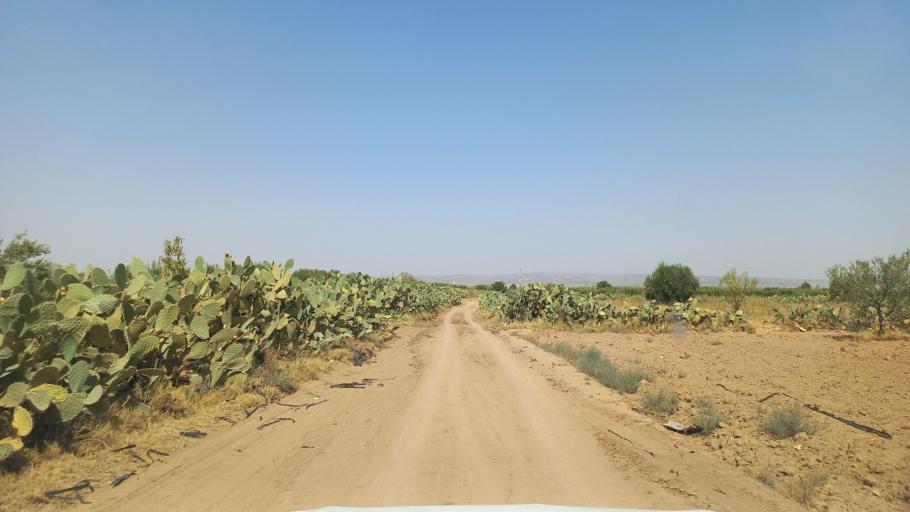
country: TN
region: Al Qasrayn
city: Kasserine
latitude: 35.2472
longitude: 9.0373
